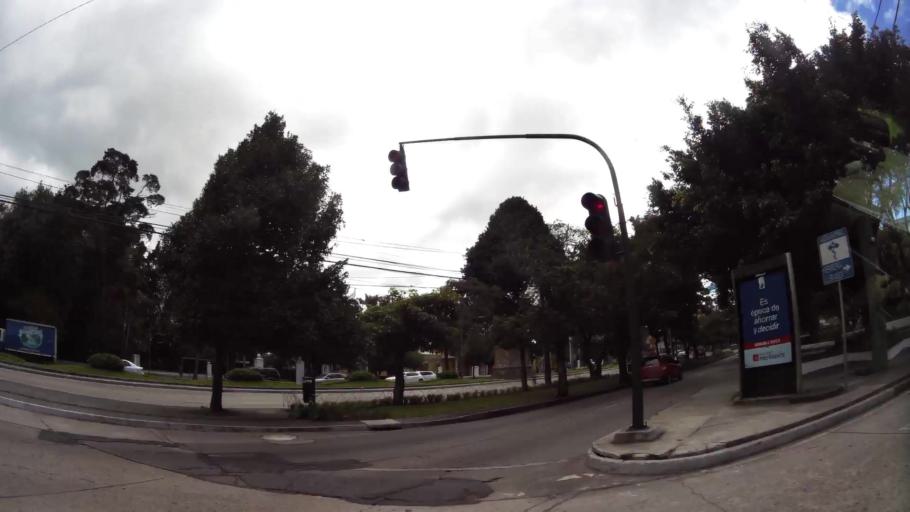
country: GT
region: Guatemala
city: Guatemala City
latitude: 14.6096
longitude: -90.5151
